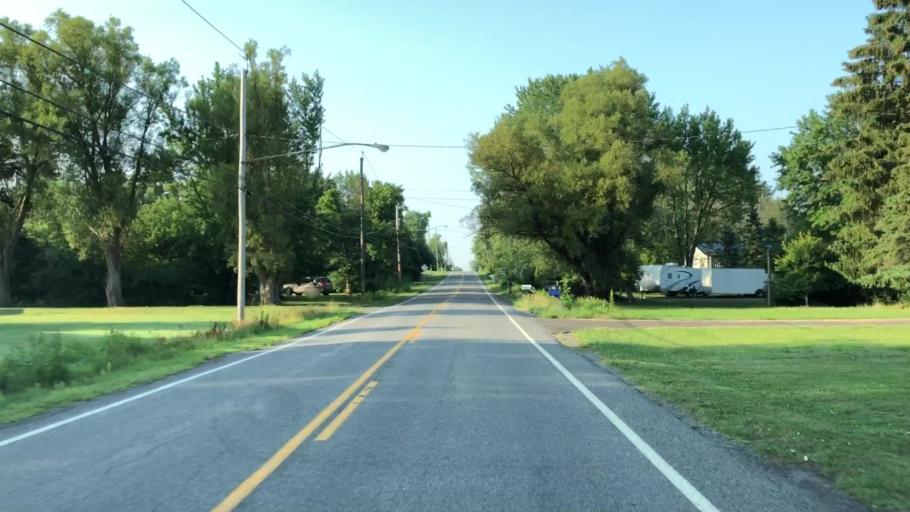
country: US
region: New York
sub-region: Erie County
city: Elma Center
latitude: 42.8454
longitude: -78.6923
